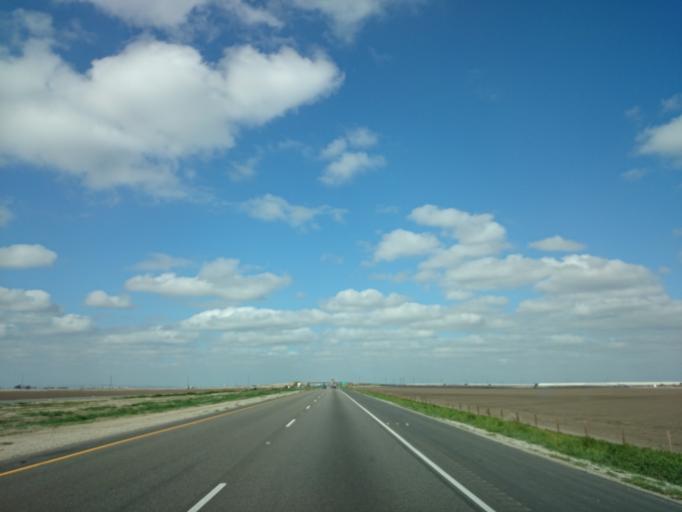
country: US
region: California
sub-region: Kern County
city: Greenfield
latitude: 35.1547
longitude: -119.1028
